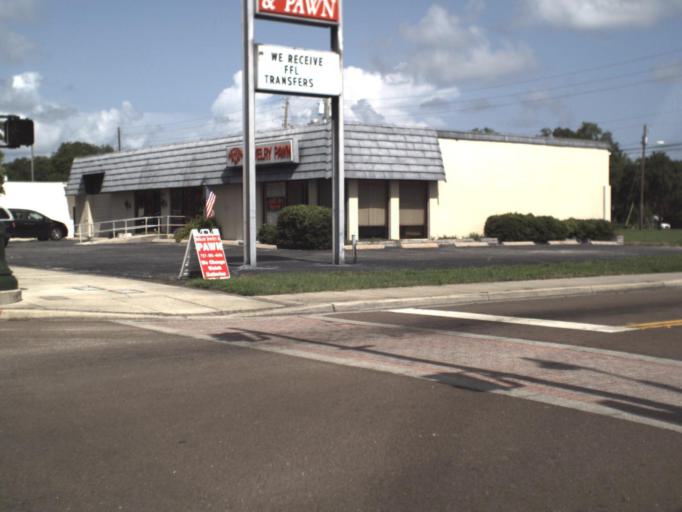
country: US
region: Florida
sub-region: Pinellas County
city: Largo
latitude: 27.9167
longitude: -82.7920
